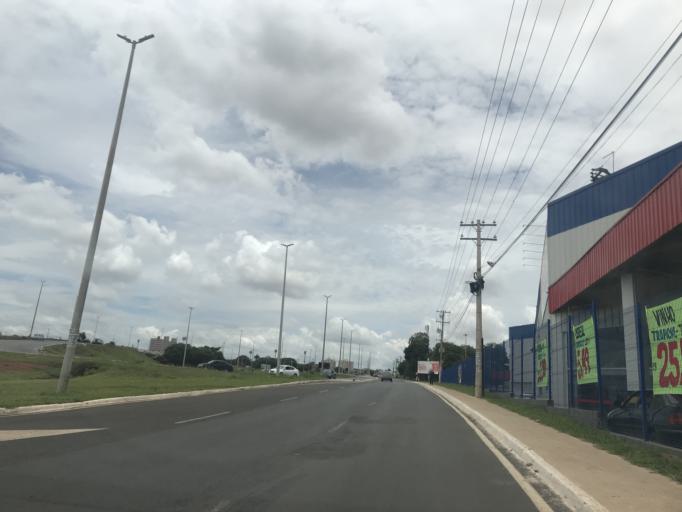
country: BR
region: Federal District
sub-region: Brasilia
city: Brasilia
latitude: -15.8345
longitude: -48.0734
